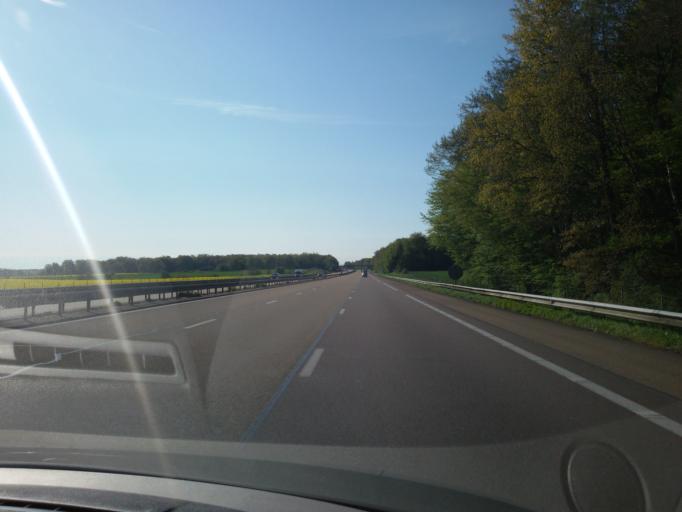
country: FR
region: Centre
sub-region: Departement du Loiret
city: Courtenay
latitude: 48.0123
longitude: 3.1495
